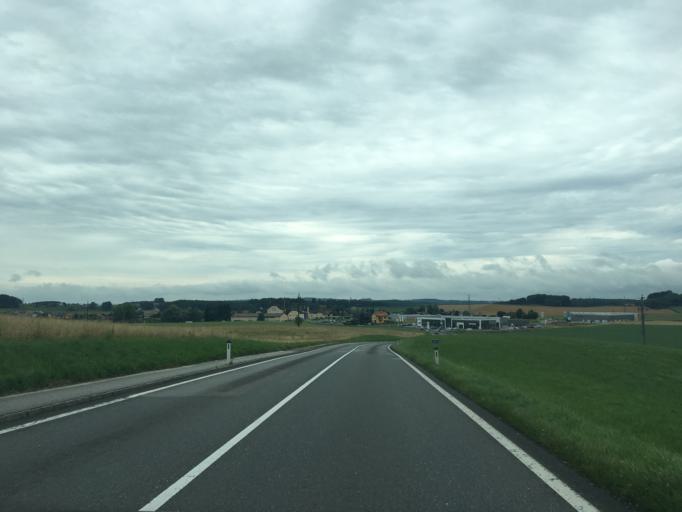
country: AT
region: Salzburg
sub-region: Politischer Bezirk Salzburg-Umgebung
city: Dorfbeuern
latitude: 48.0838
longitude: 12.9922
